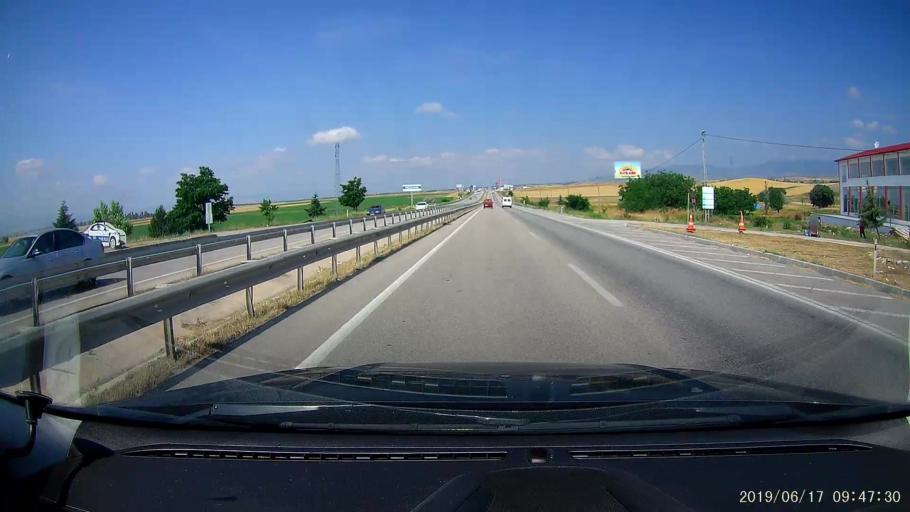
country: TR
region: Amasya
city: Suluova
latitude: 40.8764
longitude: 35.5766
